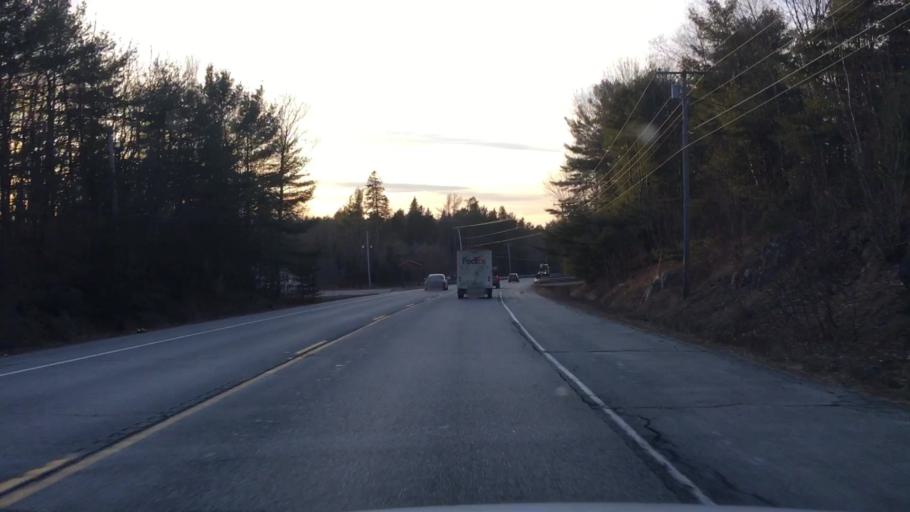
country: US
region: Maine
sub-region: Penobscot County
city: Holden
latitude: 44.7546
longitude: -68.6758
